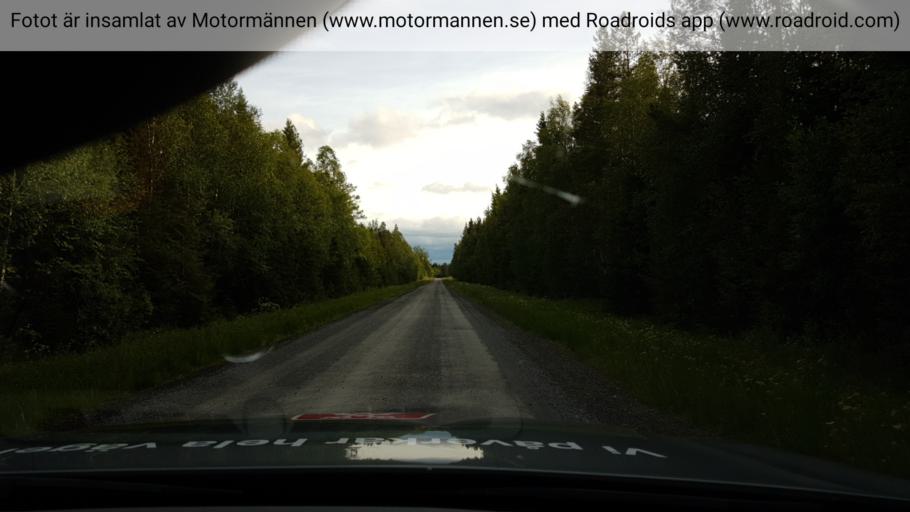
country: SE
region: Jaemtland
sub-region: Stroemsunds Kommun
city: Stroemsund
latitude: 63.7067
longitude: 15.1769
